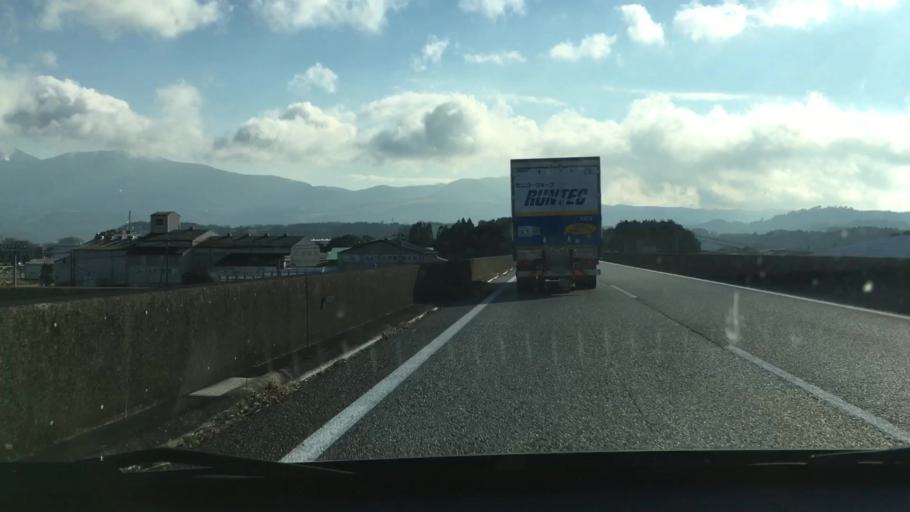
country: JP
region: Kumamoto
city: Hitoyoshi
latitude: 32.0544
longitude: 130.8022
